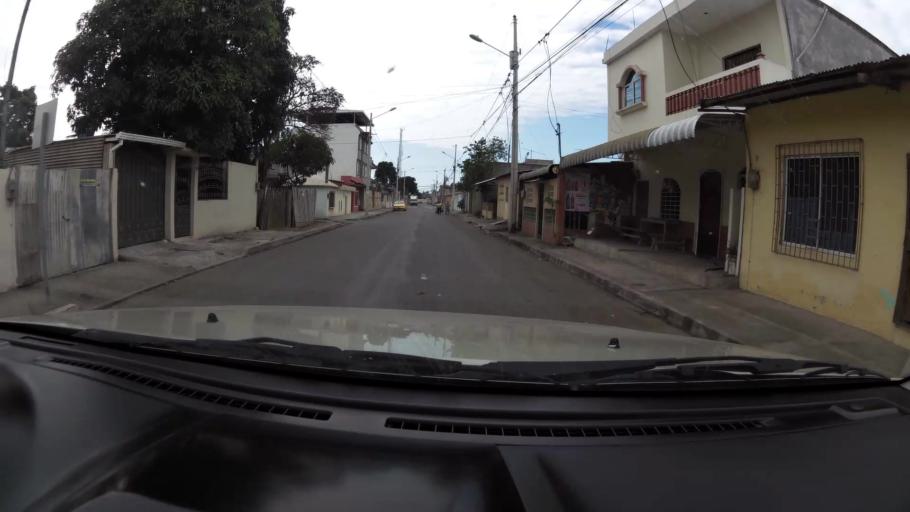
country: EC
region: El Oro
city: Machala
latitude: -3.2529
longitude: -79.9446
